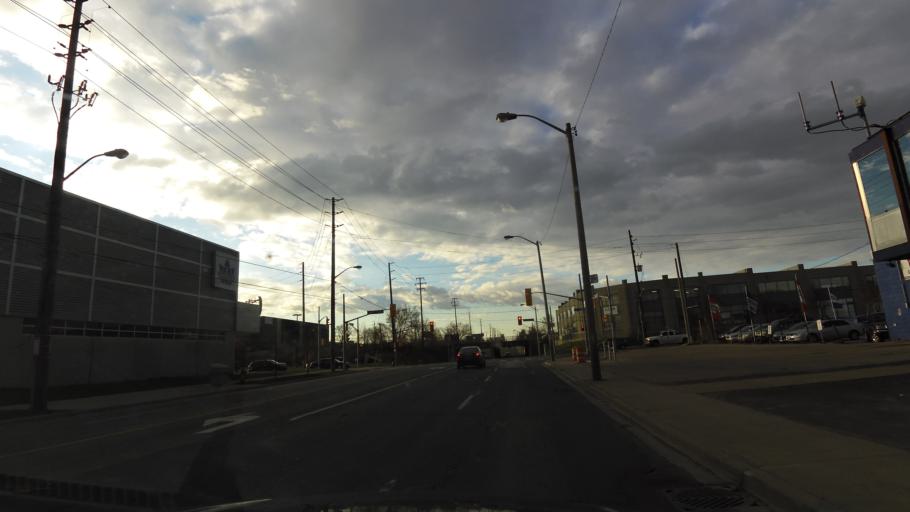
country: CA
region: Ontario
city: Etobicoke
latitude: 43.6035
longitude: -79.5191
